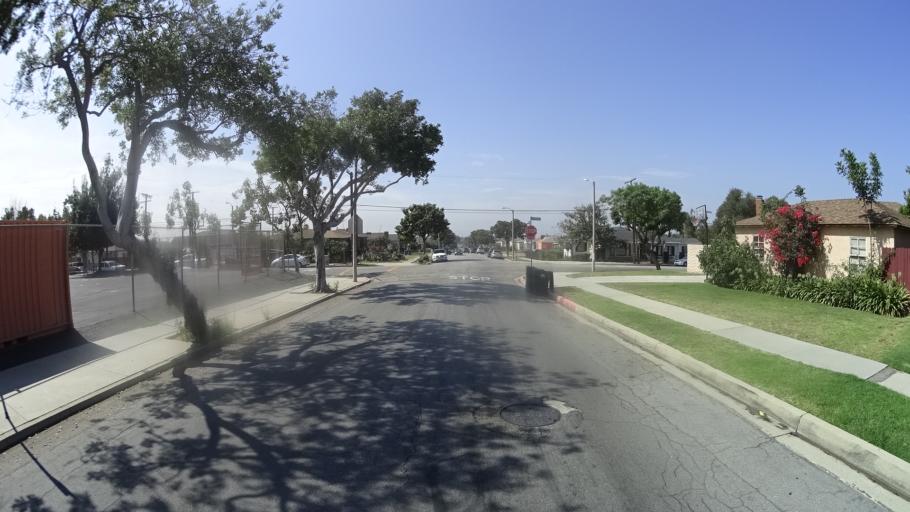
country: US
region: California
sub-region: Los Angeles County
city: View Park-Windsor Hills
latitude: 33.9912
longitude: -118.3439
